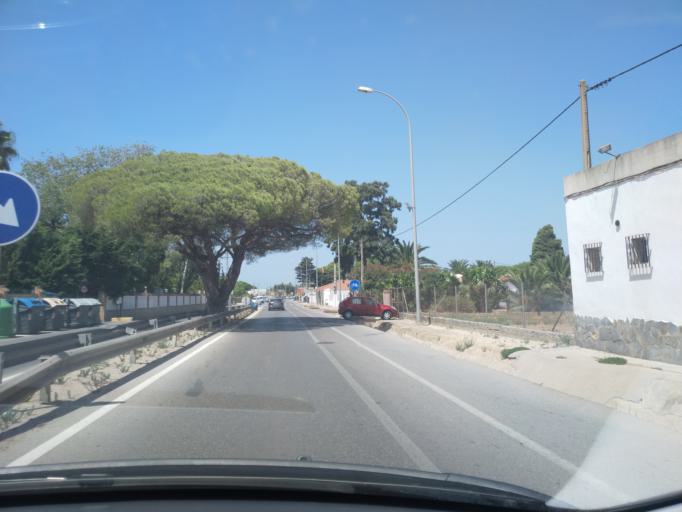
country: ES
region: Andalusia
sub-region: Provincia de Cadiz
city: Chiclana de la Frontera
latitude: 36.3942
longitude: -6.1542
